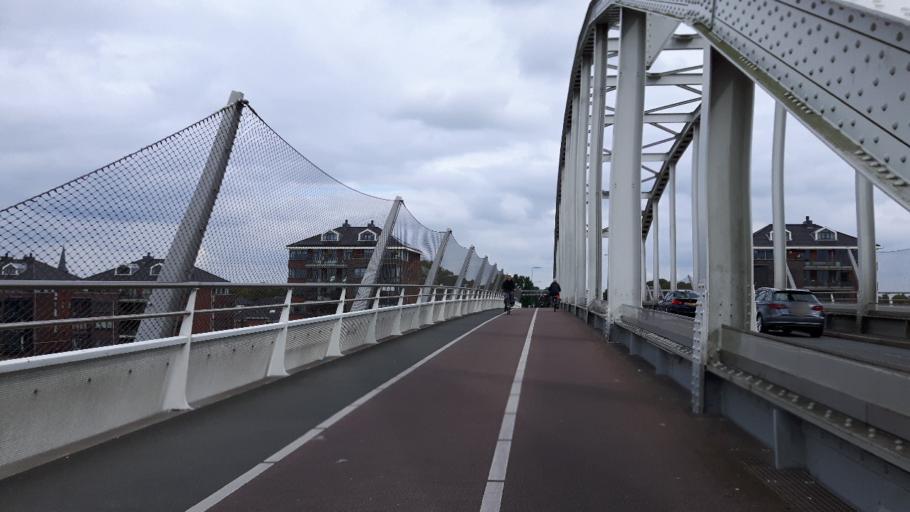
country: NL
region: Utrecht
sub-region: Stichtse Vecht
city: Maarssen
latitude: 52.1333
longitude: 5.0386
